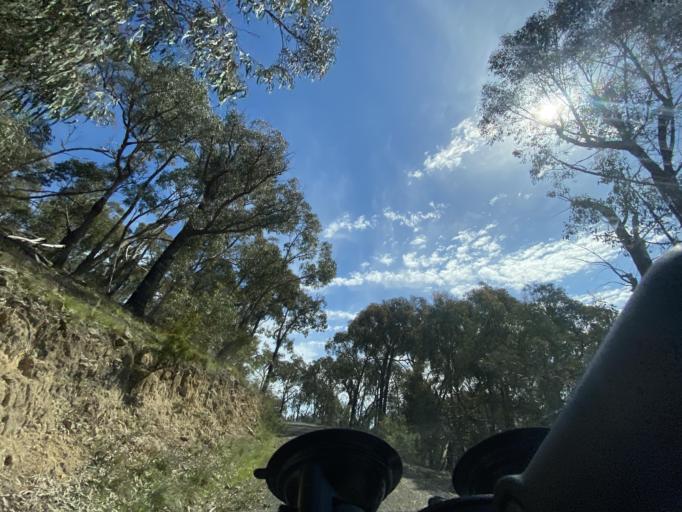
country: AU
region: Victoria
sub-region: Mansfield
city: Mansfield
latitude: -36.8081
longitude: 146.1035
